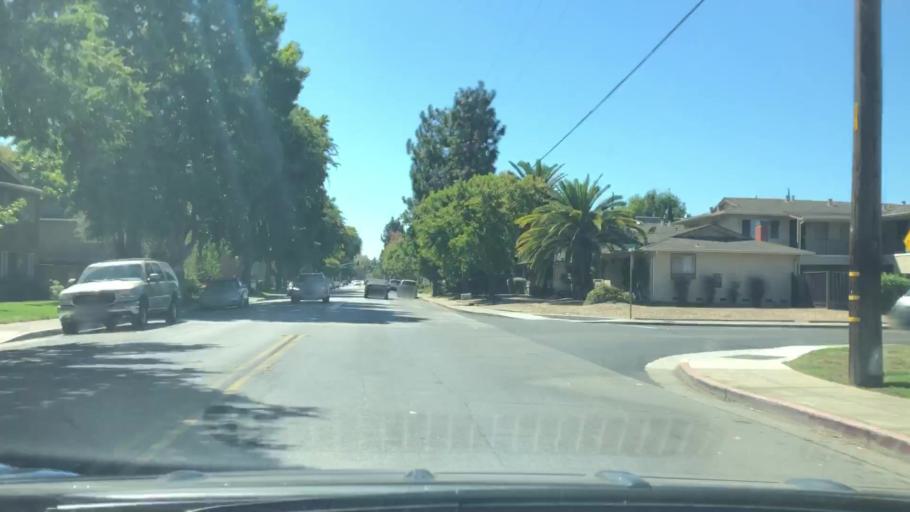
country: US
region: California
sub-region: Santa Clara County
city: Sunnyvale
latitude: 37.3548
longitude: -122.0050
